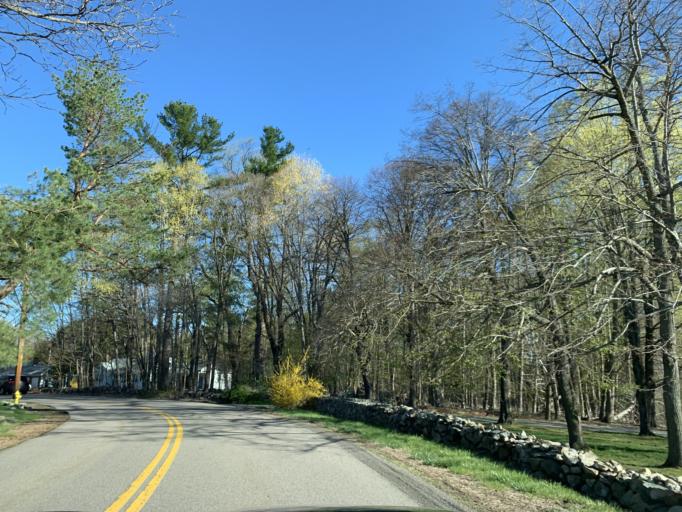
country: US
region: Massachusetts
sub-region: Norfolk County
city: Westwood
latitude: 42.2322
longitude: -71.2157
